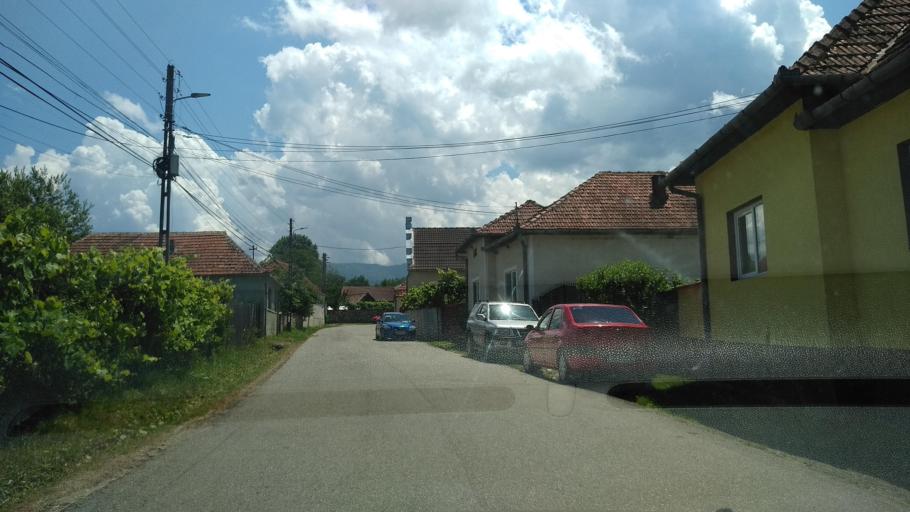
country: RO
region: Hunedoara
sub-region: Comuna Sarmizegetusa
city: Sarmizegetusa
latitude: 45.5145
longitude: 22.7815
